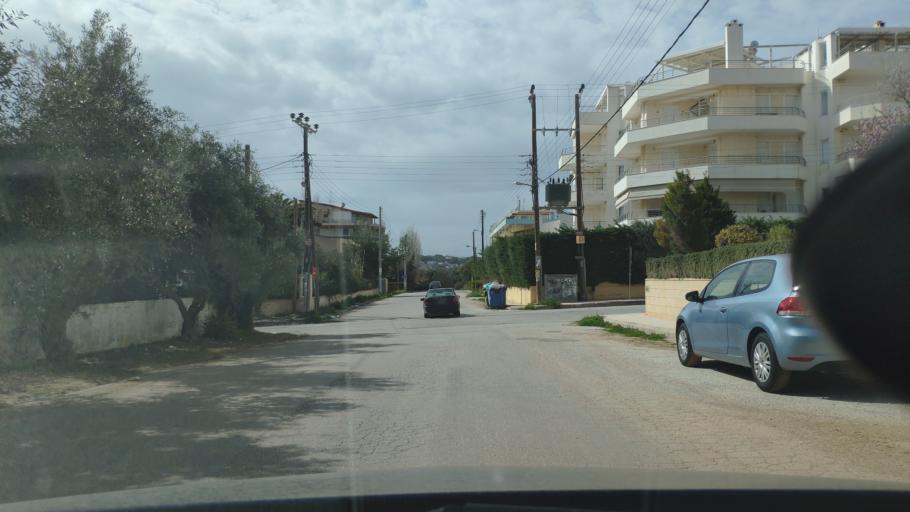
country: GR
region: Attica
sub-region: Nomarchia Anatolikis Attikis
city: Limin Mesoyaias
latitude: 37.8954
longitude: 24.0128
